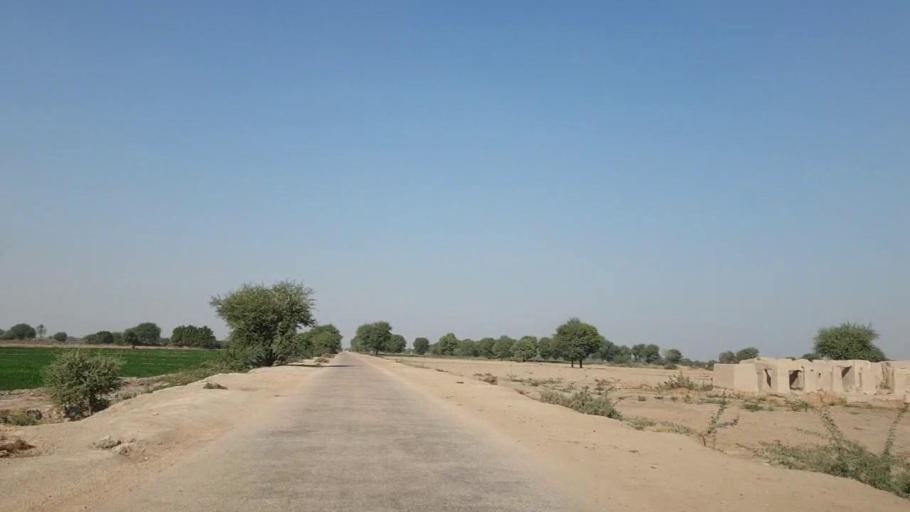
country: PK
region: Sindh
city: Digri
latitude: 25.0056
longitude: 69.1064
